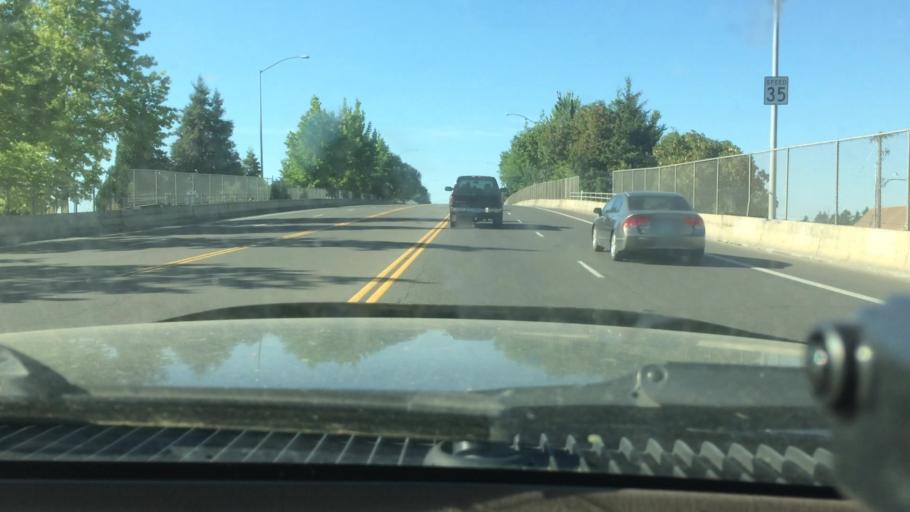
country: US
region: Oregon
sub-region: Lane County
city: Eugene
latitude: 44.0583
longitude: -123.1173
